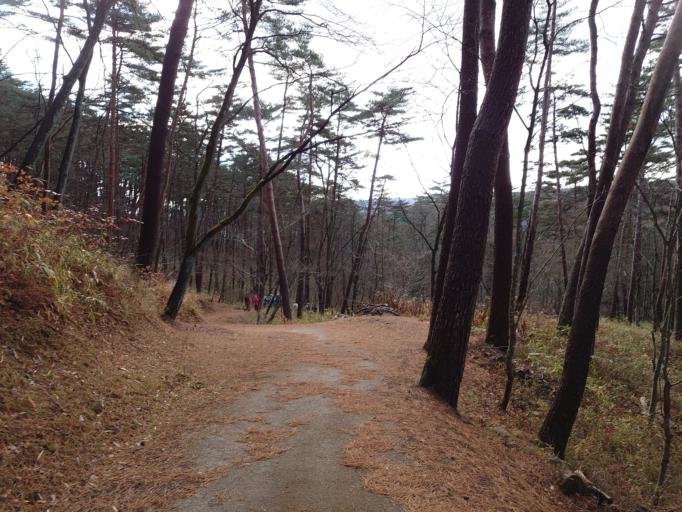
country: JP
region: Iwate
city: Ichinoseki
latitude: 38.9925
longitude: 141.1031
